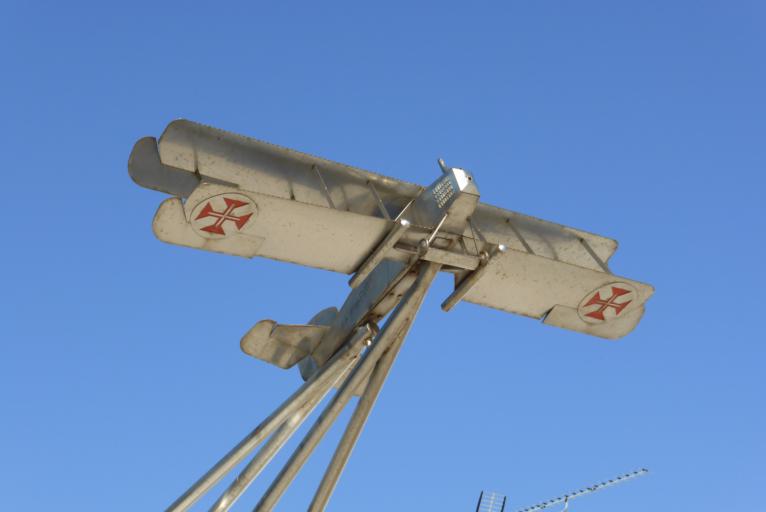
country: PT
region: Beja
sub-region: Odemira
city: Vila Nova de Milfontes
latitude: 37.7227
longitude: -8.7826
